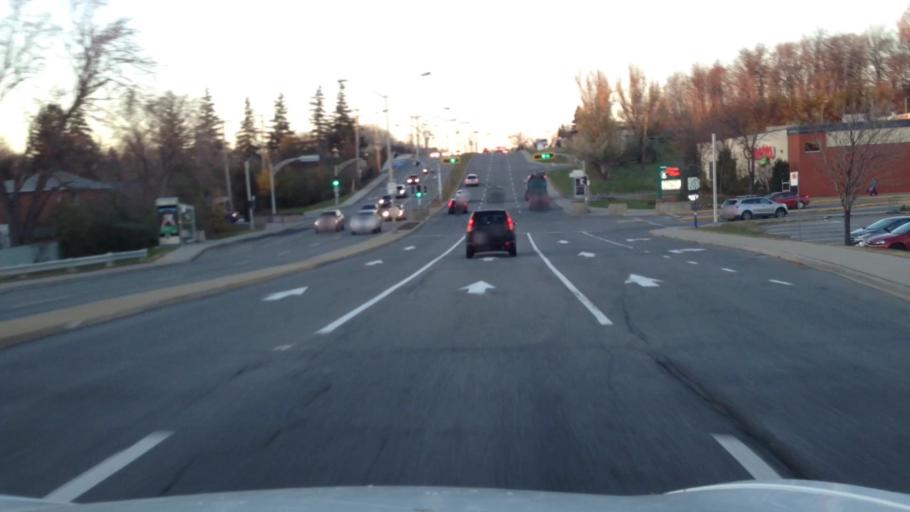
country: CA
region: Quebec
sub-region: Montreal
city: Pointe-Claire
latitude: 45.4449
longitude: -73.8161
